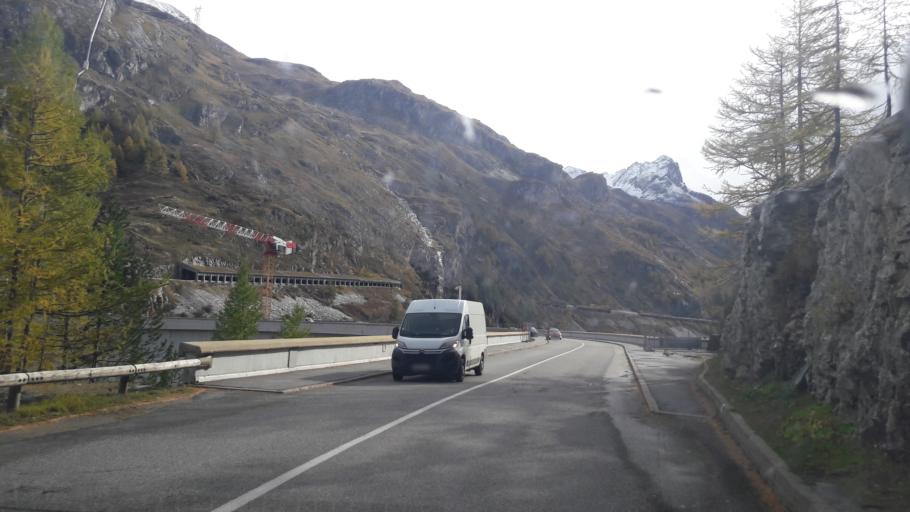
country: FR
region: Rhone-Alpes
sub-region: Departement de la Savoie
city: Tignes
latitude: 45.4952
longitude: 6.9296
